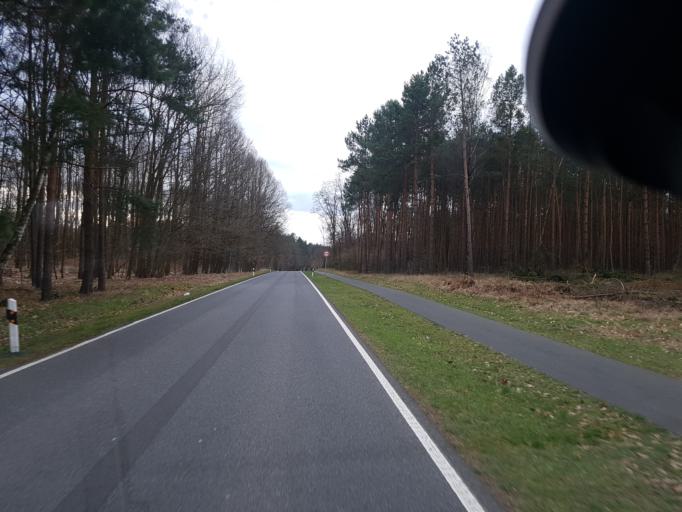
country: DE
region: Brandenburg
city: Gross Lindow
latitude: 52.1678
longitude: 14.4975
